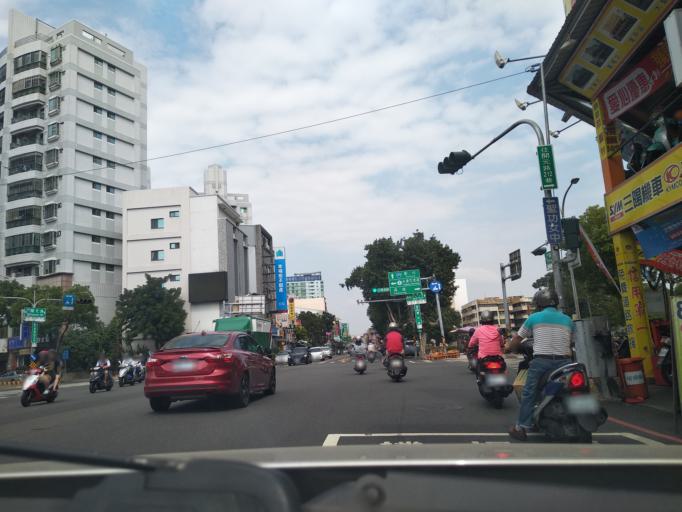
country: TW
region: Taiwan
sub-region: Tainan
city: Tainan
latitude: 23.0074
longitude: 120.2206
